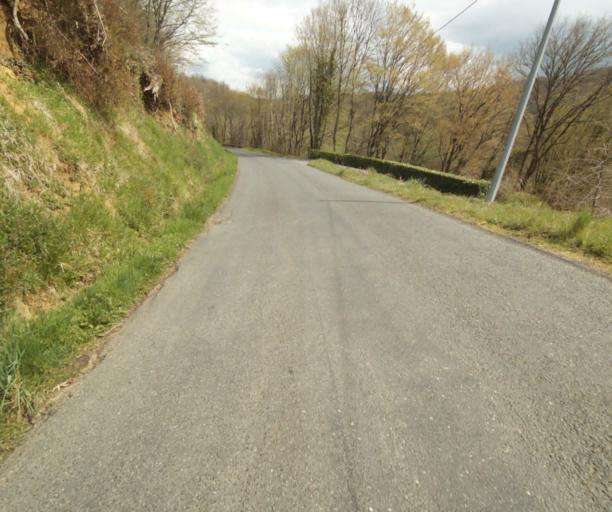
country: FR
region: Limousin
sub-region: Departement de la Correze
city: Tulle
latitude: 45.2735
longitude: 1.7955
